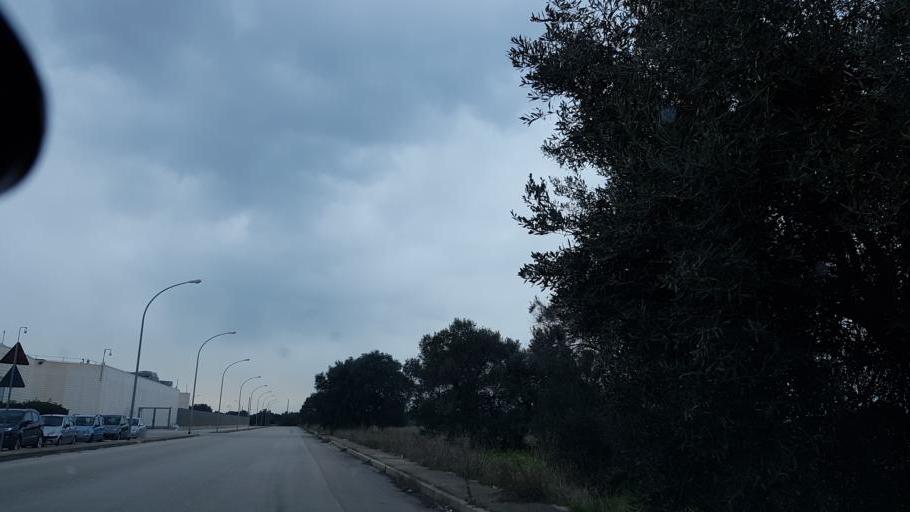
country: IT
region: Apulia
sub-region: Provincia di Brindisi
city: Mesagne
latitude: 40.5799
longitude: 17.8390
